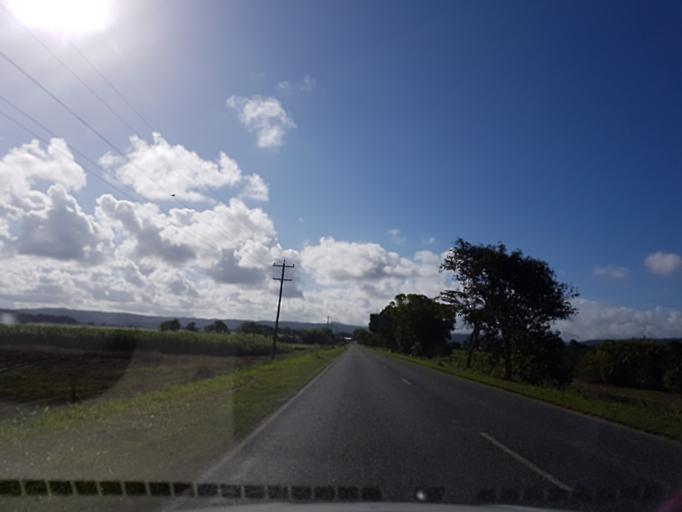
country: AU
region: Queensland
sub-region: Cairns
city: Port Douglas
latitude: -16.4122
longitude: 145.3842
